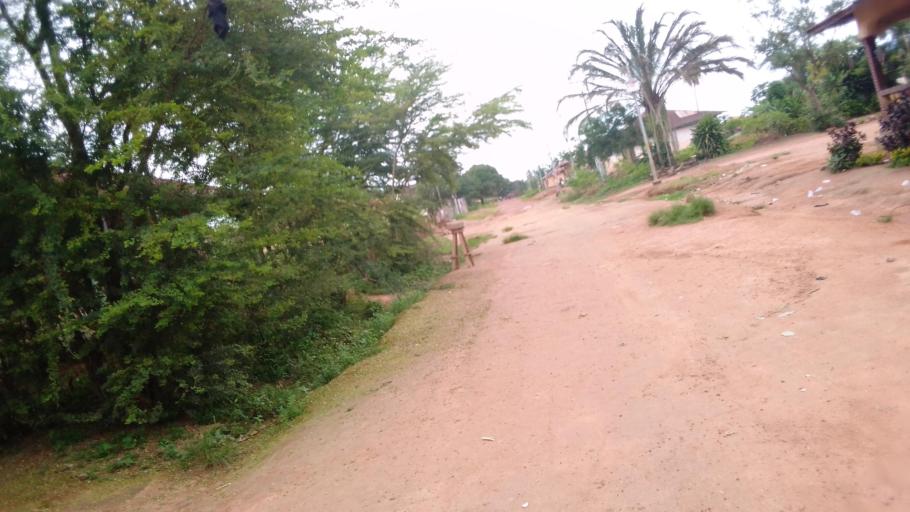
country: SL
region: Northern Province
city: Makeni
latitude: 8.8797
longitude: -12.0441
